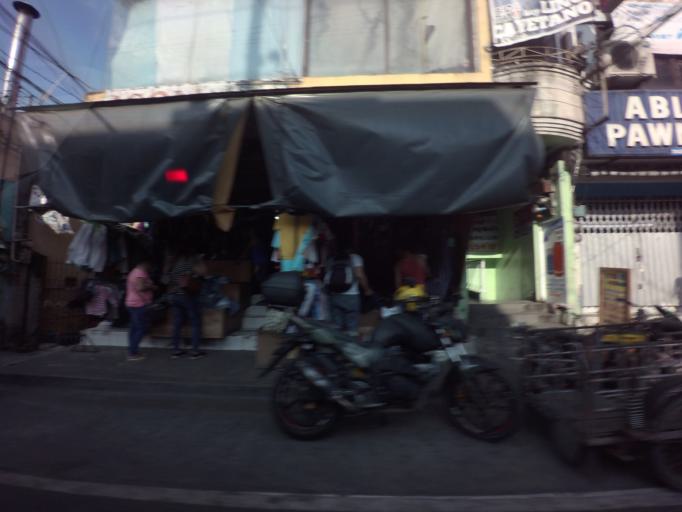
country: PH
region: Calabarzon
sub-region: Province of Rizal
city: Taguig
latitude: 14.4880
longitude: 121.0609
